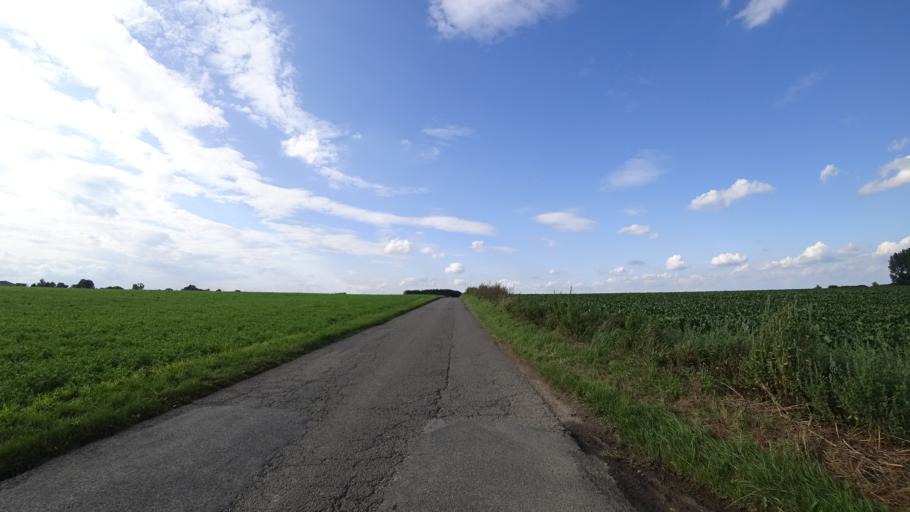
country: BE
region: Wallonia
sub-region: Province de Namur
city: Sombreffe
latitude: 50.5533
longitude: 4.6356
